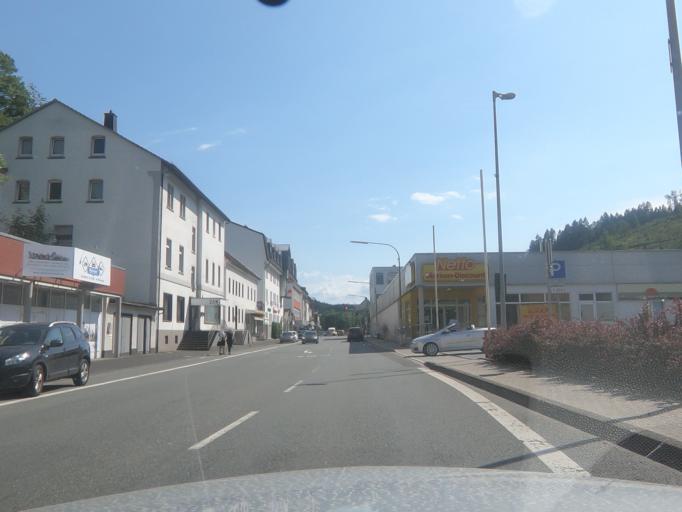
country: DE
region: North Rhine-Westphalia
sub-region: Regierungsbezirk Arnsberg
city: Finnentrop
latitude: 51.1742
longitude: 7.9657
